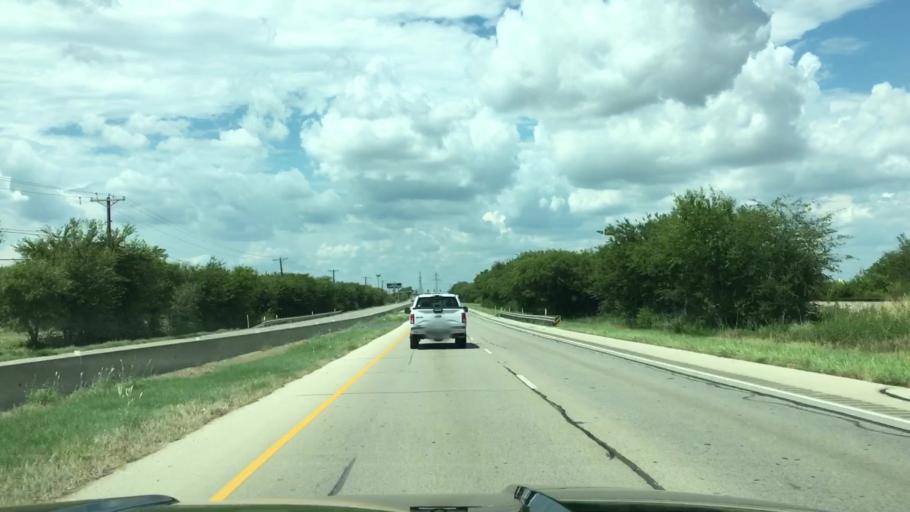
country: US
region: Texas
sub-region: Tarrant County
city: Saginaw
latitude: 32.8958
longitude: -97.3947
